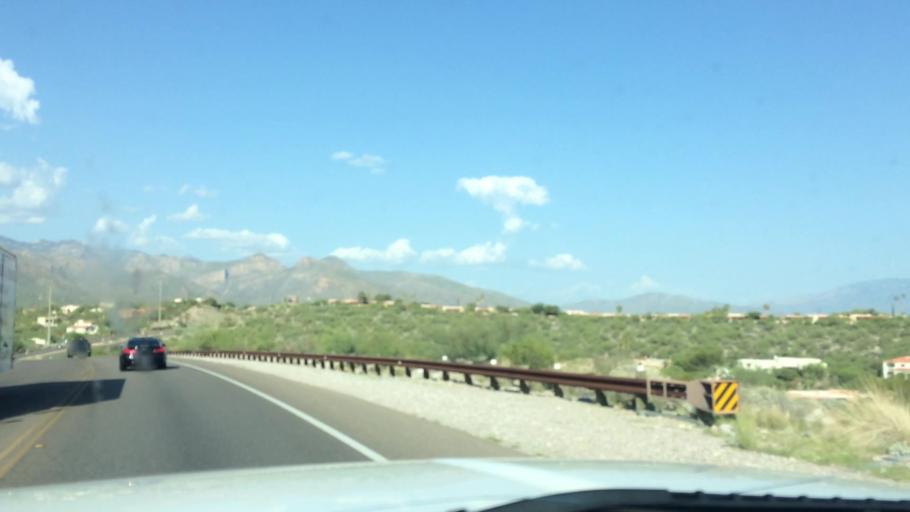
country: US
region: Arizona
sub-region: Pima County
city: Catalina Foothills
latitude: 32.3065
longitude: -110.8636
